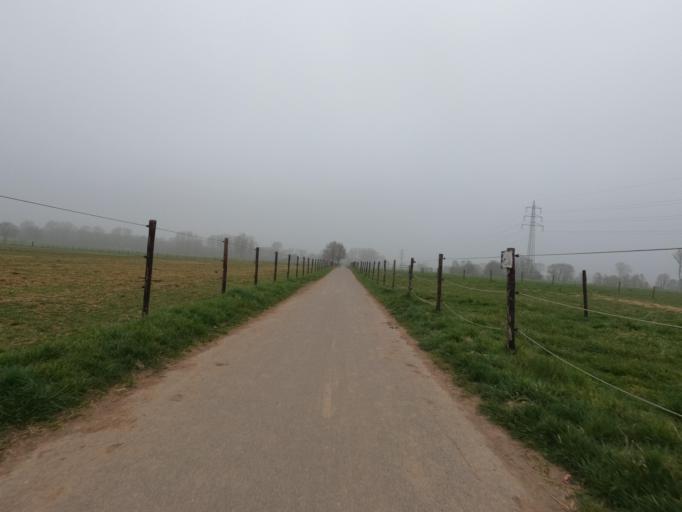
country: DE
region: North Rhine-Westphalia
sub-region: Regierungsbezirk Koln
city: Wassenberg
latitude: 51.0638
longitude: 6.1563
